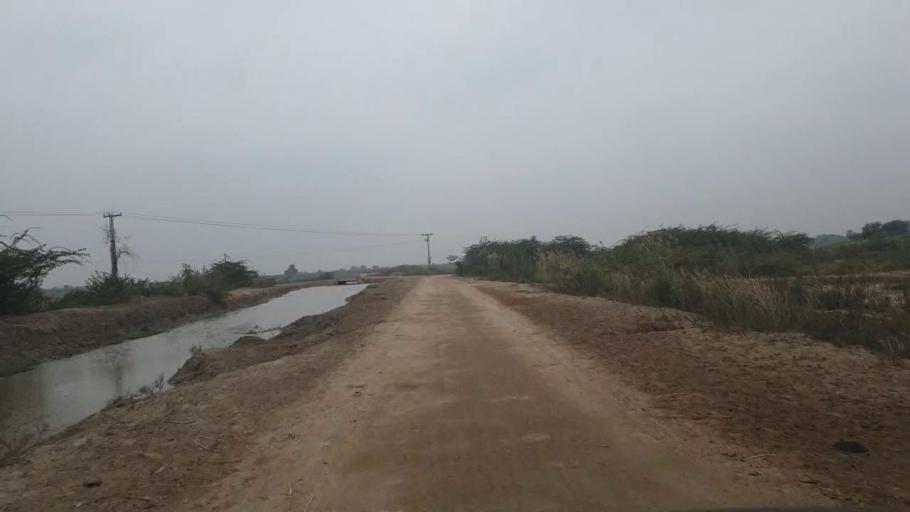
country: PK
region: Sindh
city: Tando Adam
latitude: 25.8329
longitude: 68.7204
